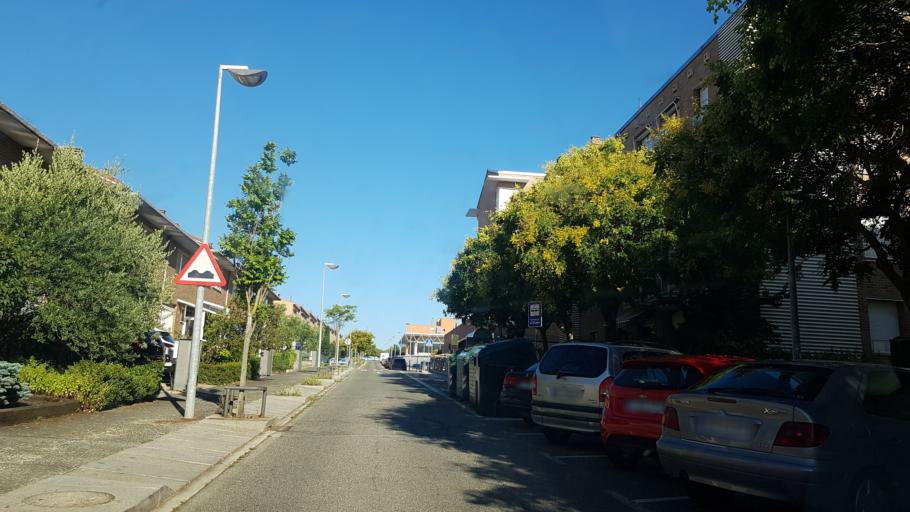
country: ES
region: Navarre
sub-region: Provincia de Navarra
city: Burlata
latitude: 42.8073
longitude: -1.6155
